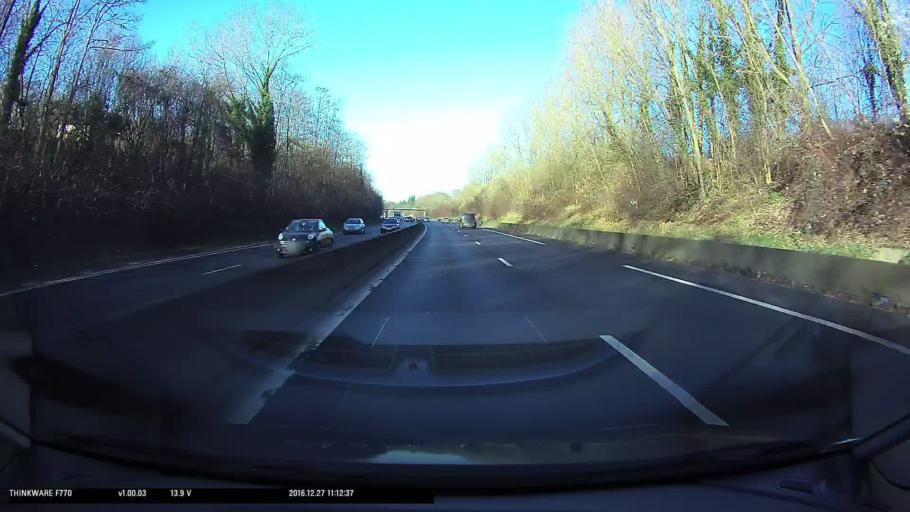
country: FR
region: Ile-de-France
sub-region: Departement du Val-d'Oise
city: Osny
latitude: 49.0512
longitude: 2.0665
